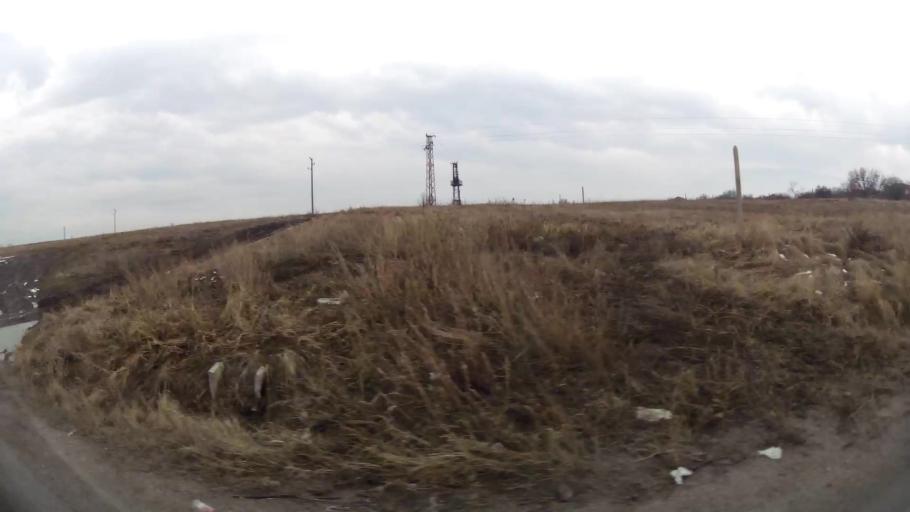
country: BG
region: Sofiya
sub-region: Obshtina Bozhurishte
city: Bozhurishte
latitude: 42.7007
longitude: 23.2203
